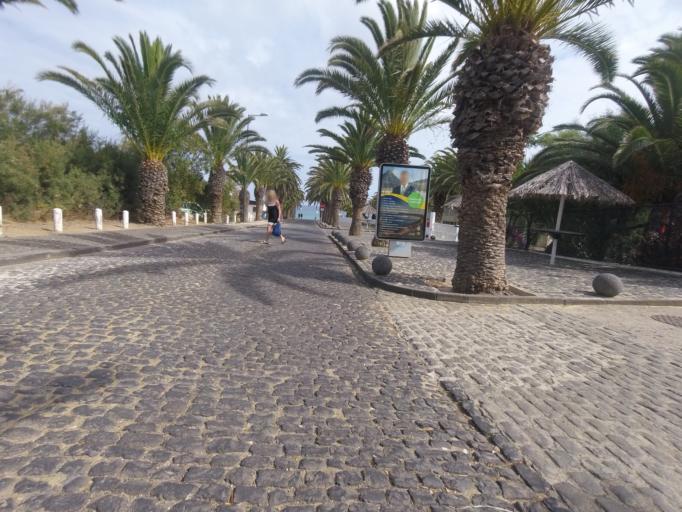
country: PT
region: Madeira
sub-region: Porto Santo
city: Vila de Porto Santo
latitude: 33.0572
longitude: -16.3383
